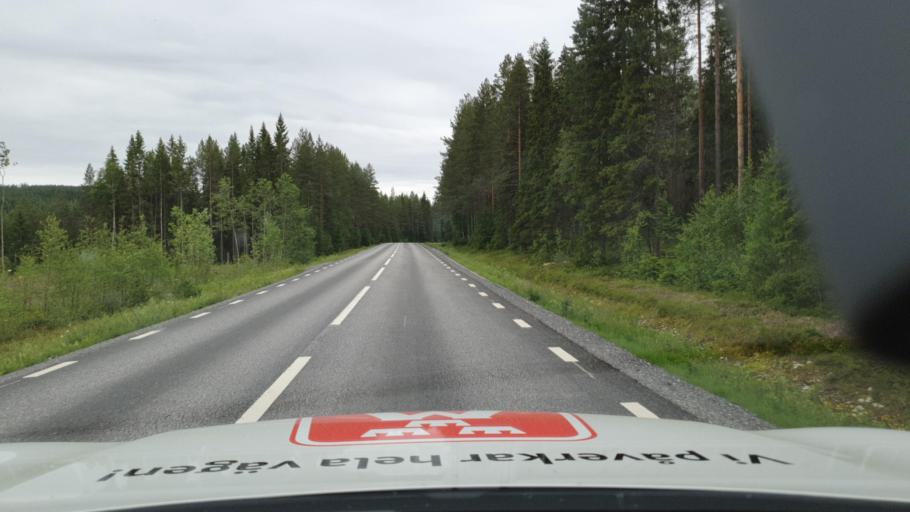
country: SE
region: Vaesterbotten
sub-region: Vannas Kommun
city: Vaennaes
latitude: 63.7290
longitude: 19.6516
